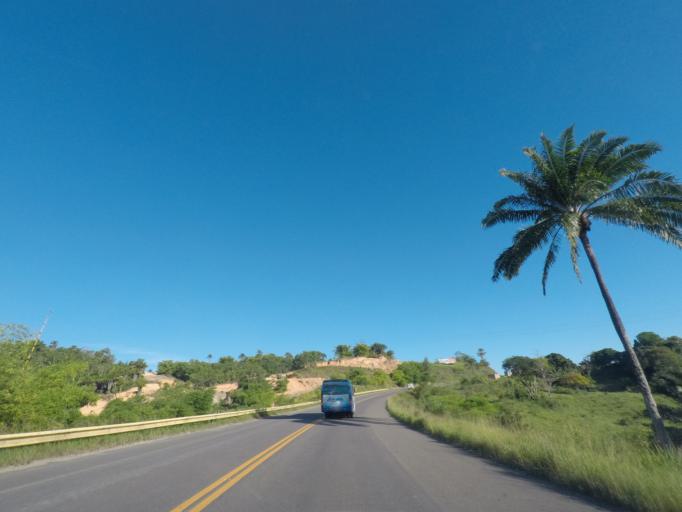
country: BR
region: Bahia
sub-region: Nazare
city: Nazare
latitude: -13.0253
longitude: -38.9971
